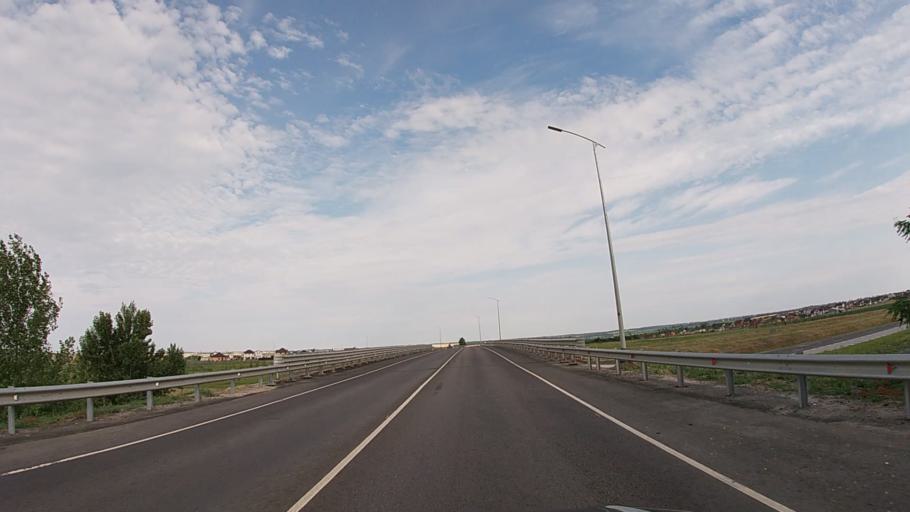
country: RU
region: Belgorod
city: Severnyy
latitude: 50.6747
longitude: 36.4736
